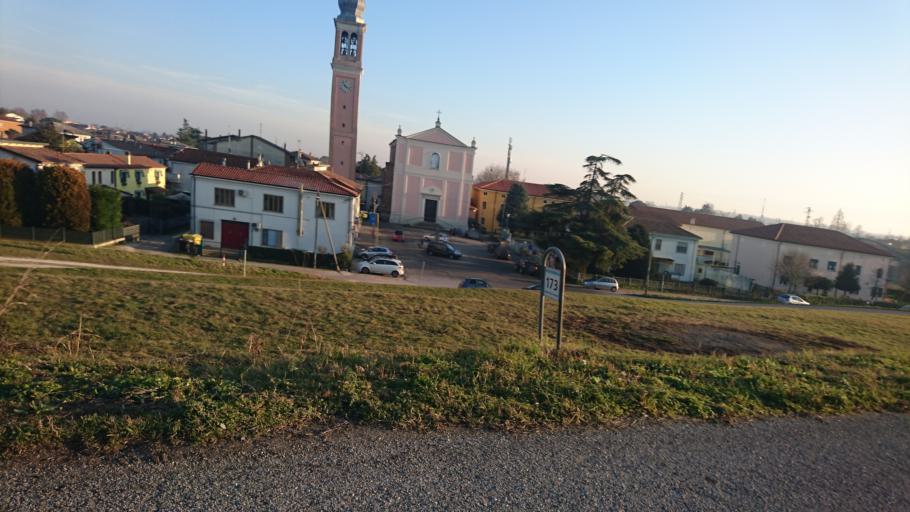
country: IT
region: Veneto
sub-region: Provincia di Padova
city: Boara Pisani
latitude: 45.1066
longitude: 11.7865
